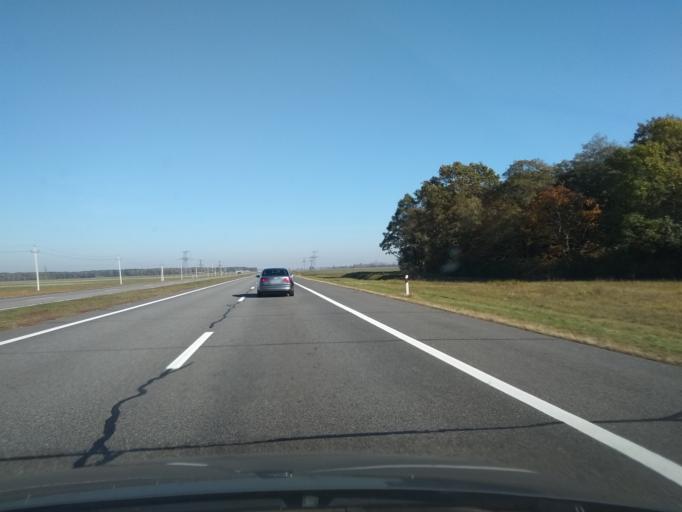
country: BY
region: Brest
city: Antopal'
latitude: 52.3993
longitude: 24.7911
